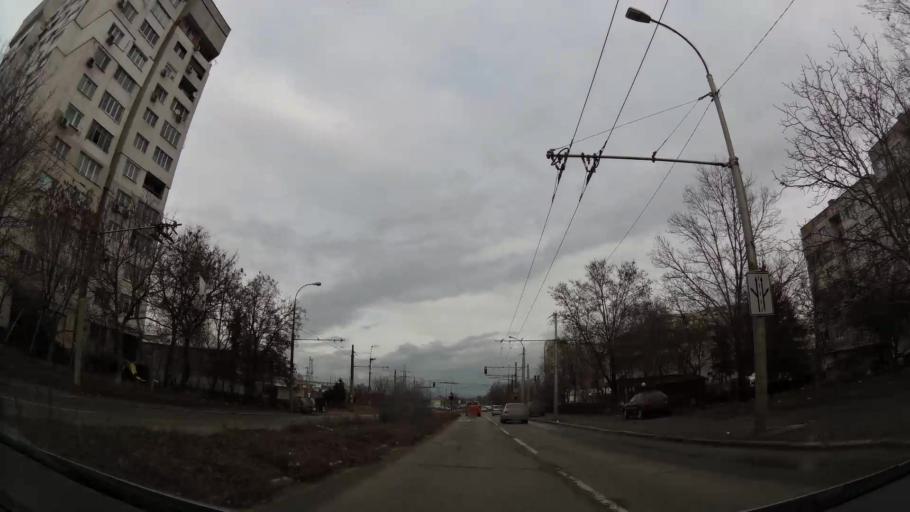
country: BG
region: Sofiya
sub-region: Obshtina Bozhurishte
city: Bozhurishte
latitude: 42.7287
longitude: 23.2468
